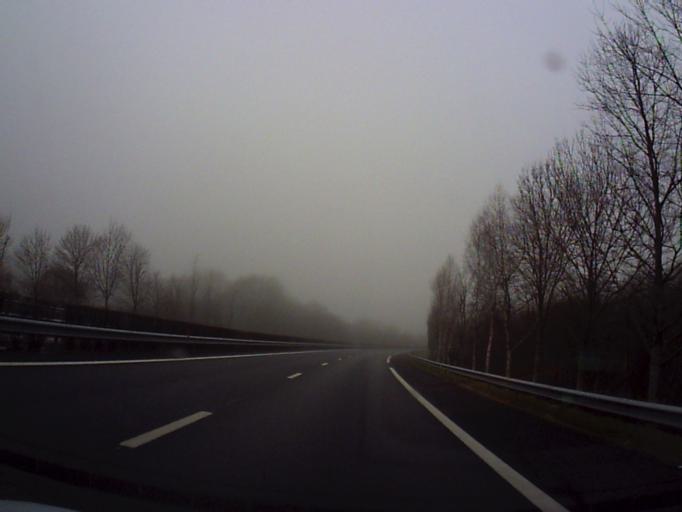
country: FR
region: Brittany
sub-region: Departement du Morbihan
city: Augan
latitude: 47.9242
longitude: -2.2352
